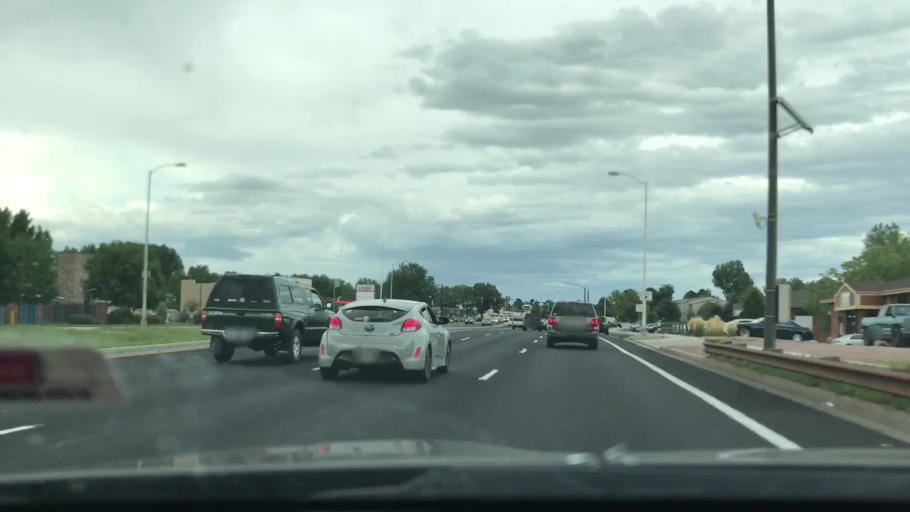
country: US
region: Colorado
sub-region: El Paso County
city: Colorado Springs
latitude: 38.8898
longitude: -104.7692
